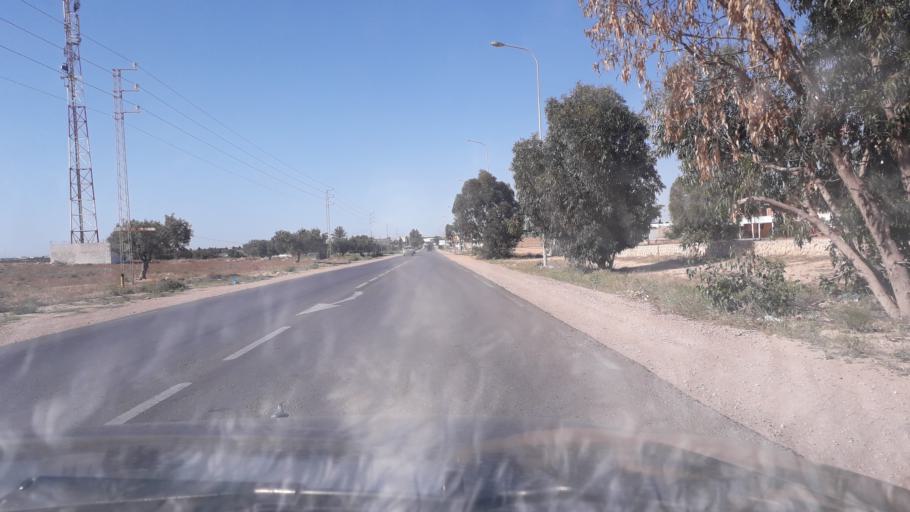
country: TN
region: Safaqis
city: Al Qarmadah
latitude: 34.8842
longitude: 10.7612
